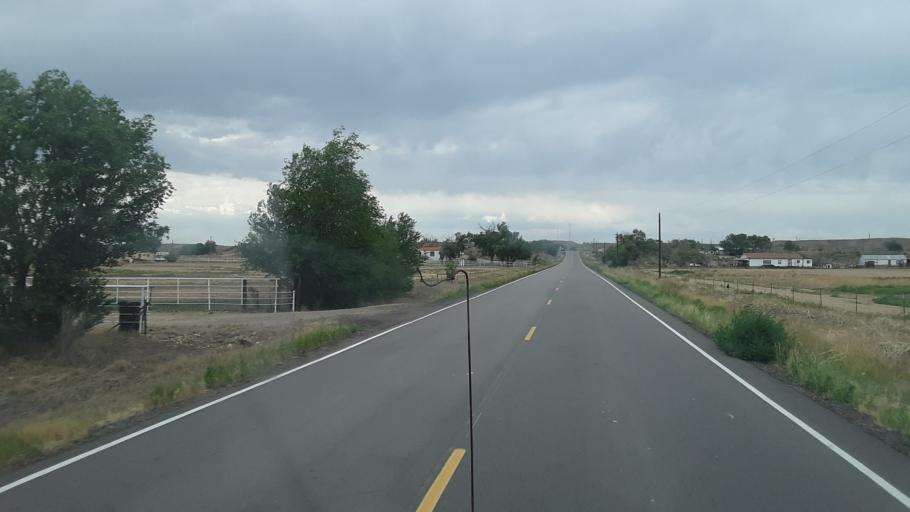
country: US
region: Colorado
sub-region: Otero County
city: Fowler
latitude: 38.1501
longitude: -104.0231
